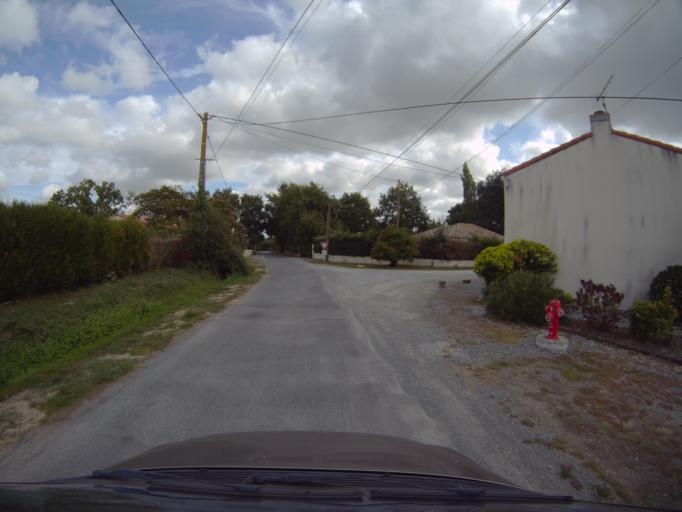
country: FR
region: Pays de la Loire
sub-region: Departement de la Loire-Atlantique
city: La Planche
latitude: 47.0250
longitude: -1.4101
